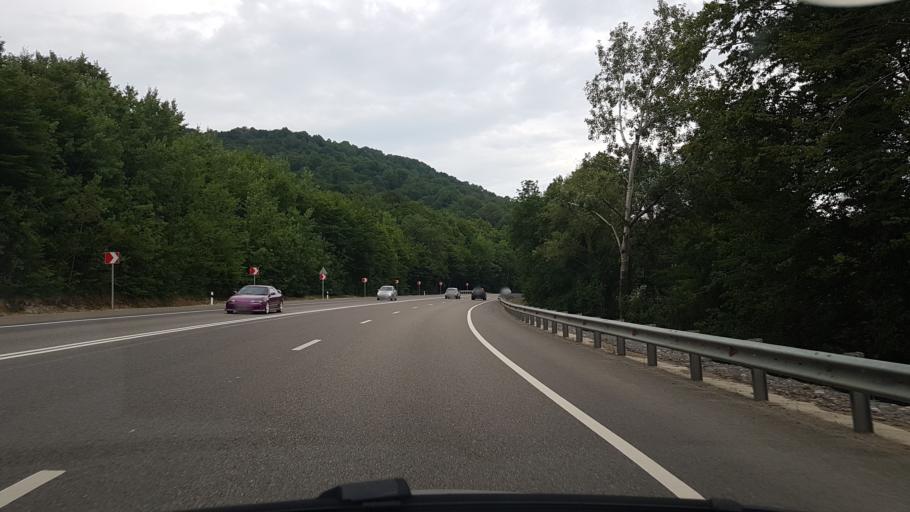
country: RU
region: Krasnodarskiy
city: Dzhubga
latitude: 44.3996
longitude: 38.7381
